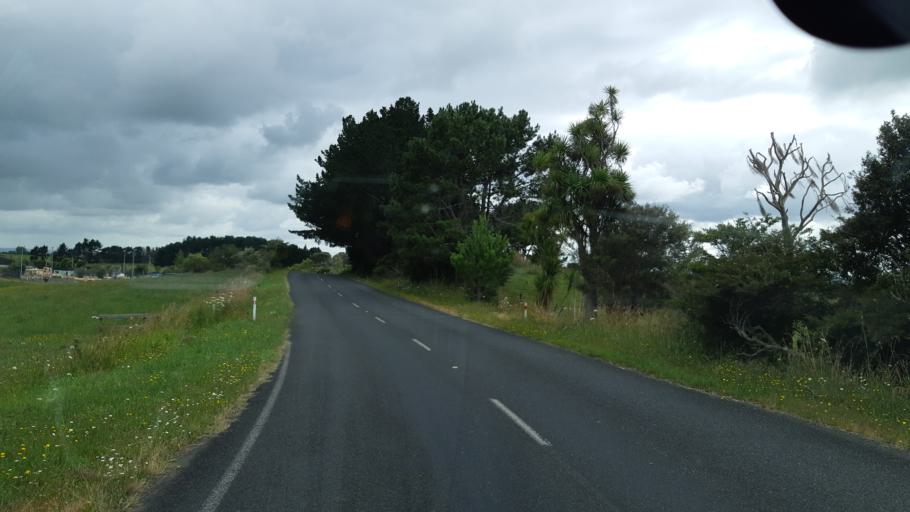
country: NZ
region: Waikato
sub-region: Waikato District
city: Ngaruawahia
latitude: -37.5615
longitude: 175.0649
